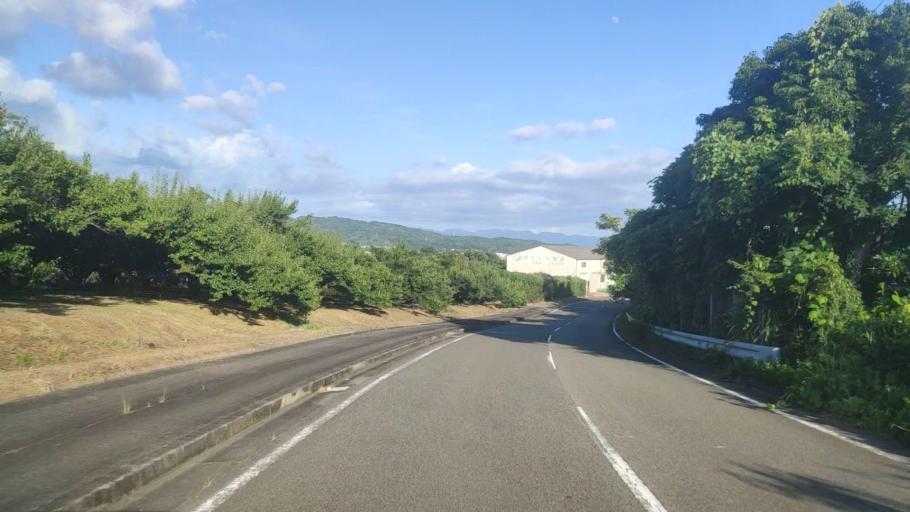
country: JP
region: Wakayama
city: Tanabe
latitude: 33.7773
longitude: 135.3032
